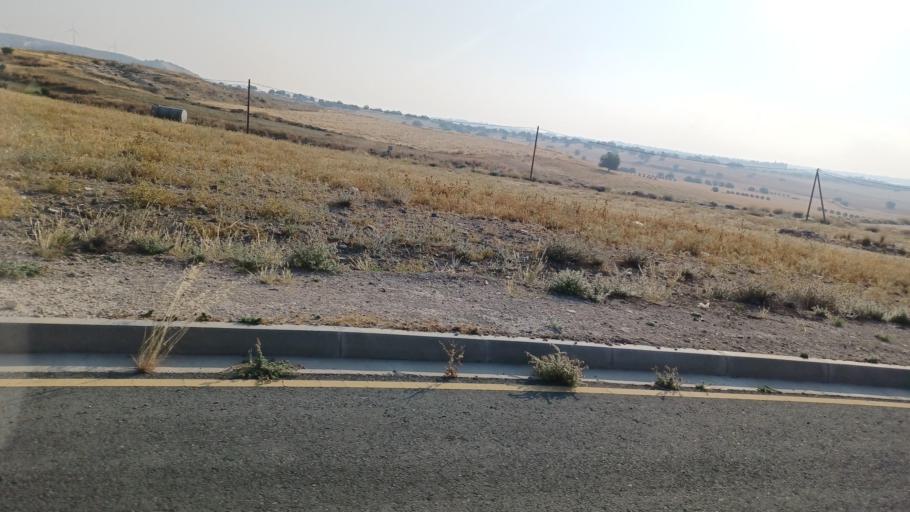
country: CY
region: Larnaka
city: Tersefanou
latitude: 34.8366
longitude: 33.5148
